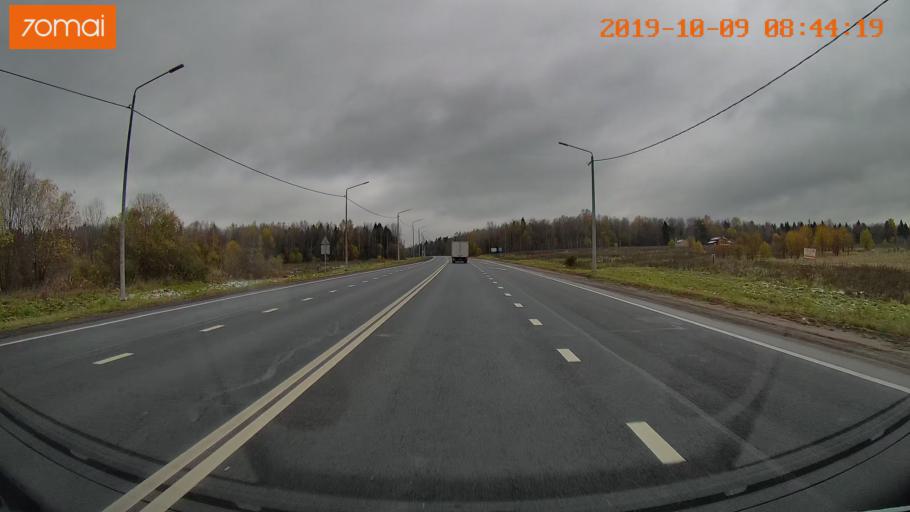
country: RU
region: Vologda
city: Gryazovets
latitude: 59.0349
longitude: 40.1088
